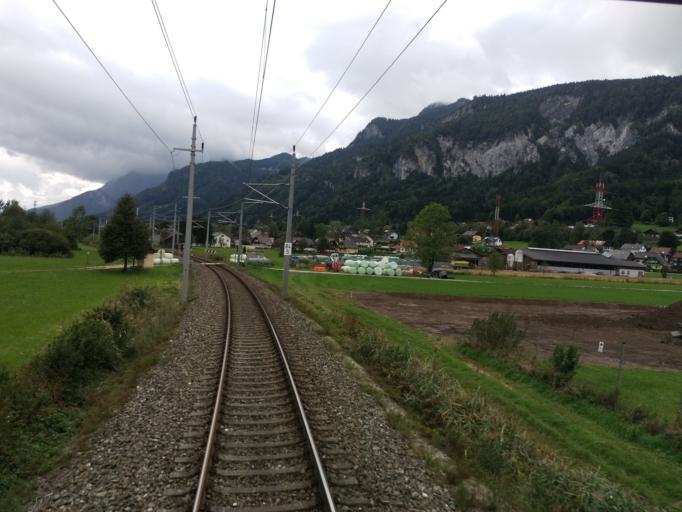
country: AT
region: Styria
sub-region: Politischer Bezirk Liezen
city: Worschach
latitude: 47.5482
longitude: 14.1477
